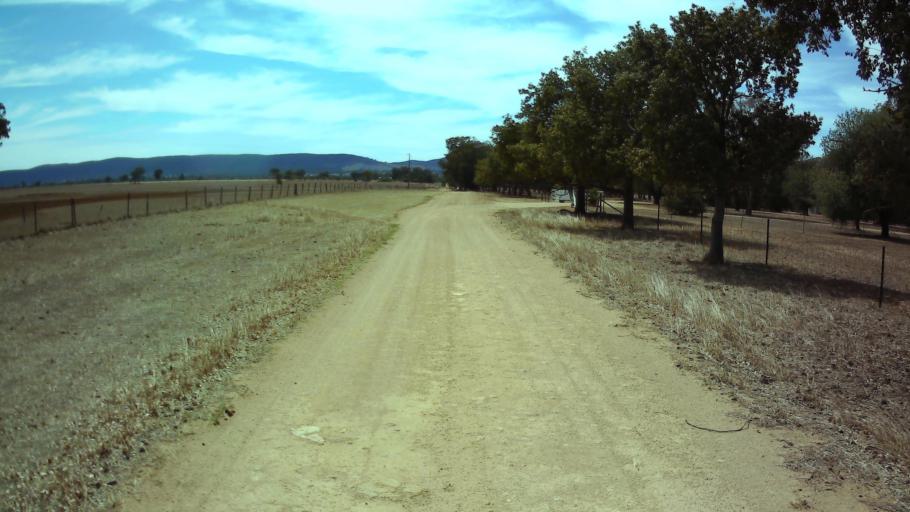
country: AU
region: New South Wales
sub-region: Weddin
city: Grenfell
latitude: -33.7214
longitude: 148.2632
